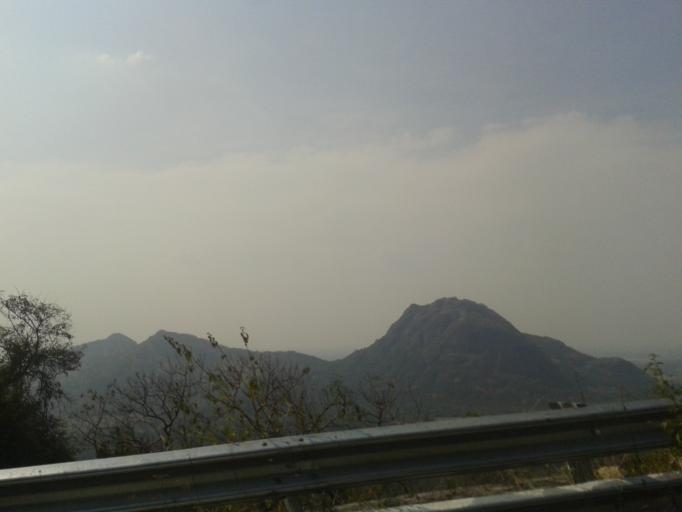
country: IN
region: Tamil Nadu
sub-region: Dindigul
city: Palani
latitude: 10.3620
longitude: 77.5273
